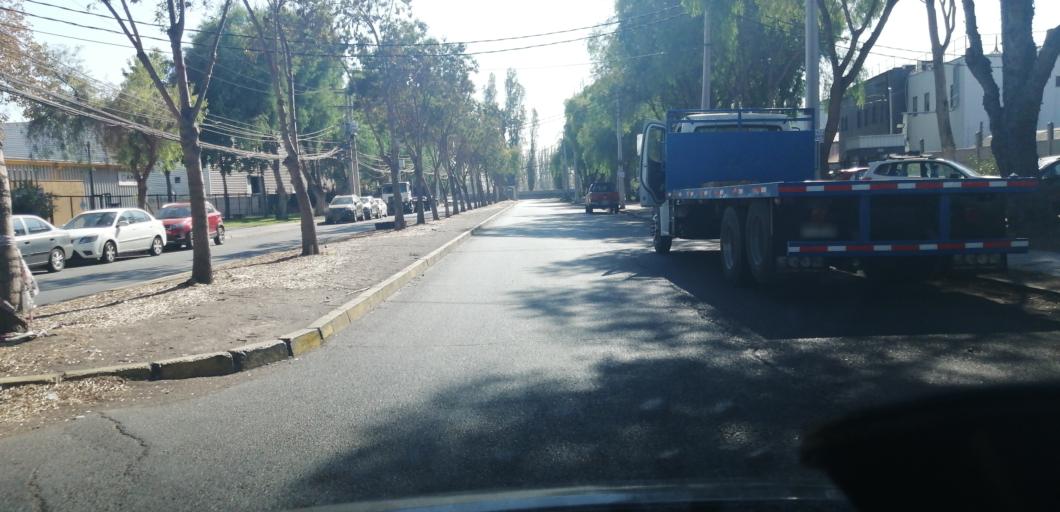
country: CL
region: Santiago Metropolitan
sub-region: Provincia de Santiago
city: Lo Prado
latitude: -33.3807
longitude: -70.7731
